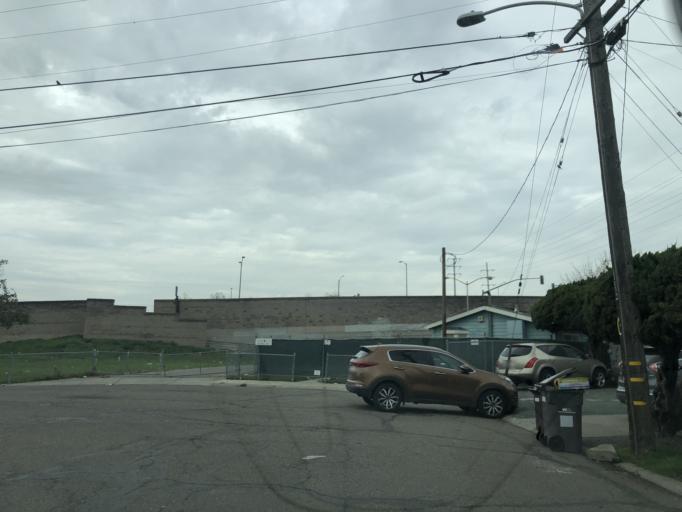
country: US
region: California
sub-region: Alameda County
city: San Leandro
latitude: 37.7302
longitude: -122.1898
